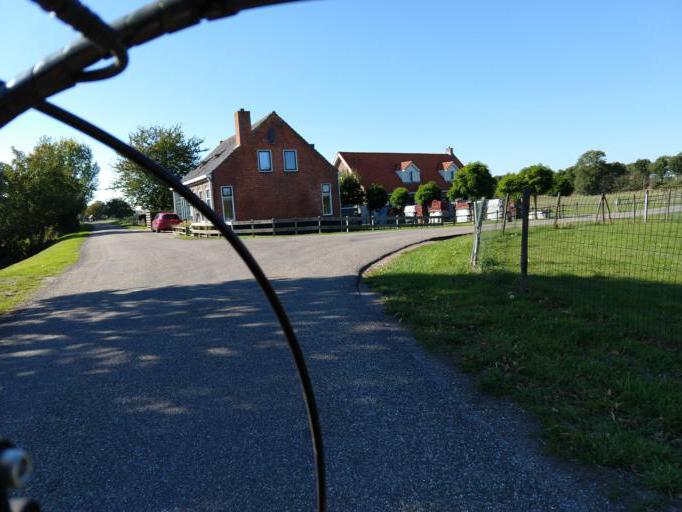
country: NL
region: Zeeland
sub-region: Gemeente Goes
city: Goes
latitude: 51.4362
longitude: 3.8275
